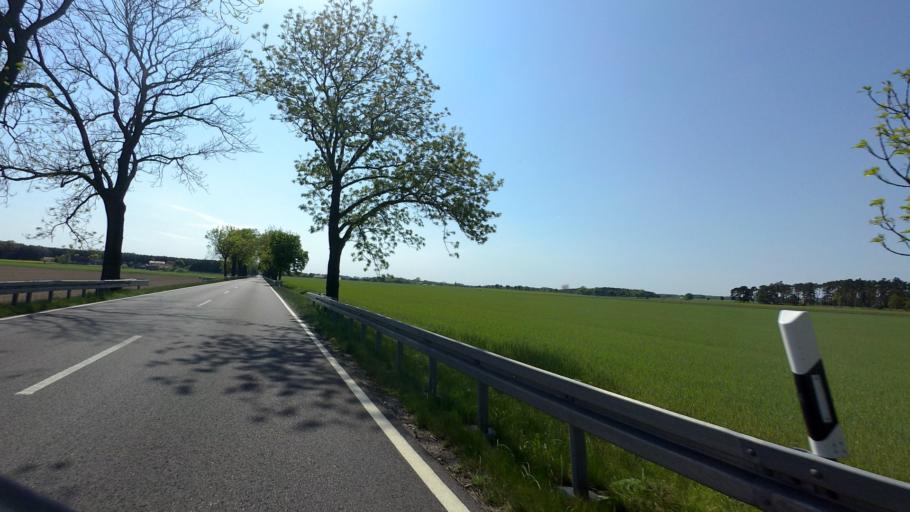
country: DE
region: Brandenburg
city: Neu Zauche
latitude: 52.0348
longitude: 14.0997
